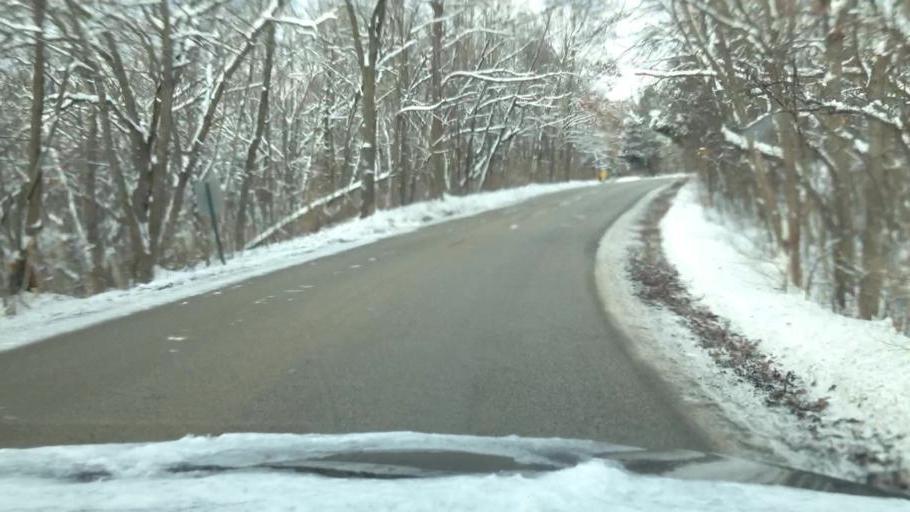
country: US
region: Wisconsin
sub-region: Walworth County
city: East Troy
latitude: 42.8061
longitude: -88.4255
